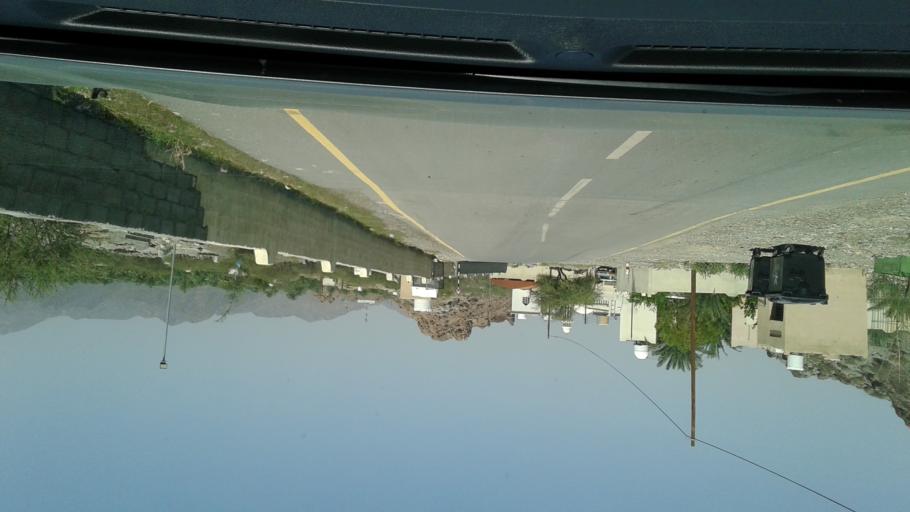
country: OM
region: Al Batinah
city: Rustaq
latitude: 23.3914
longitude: 57.4100
